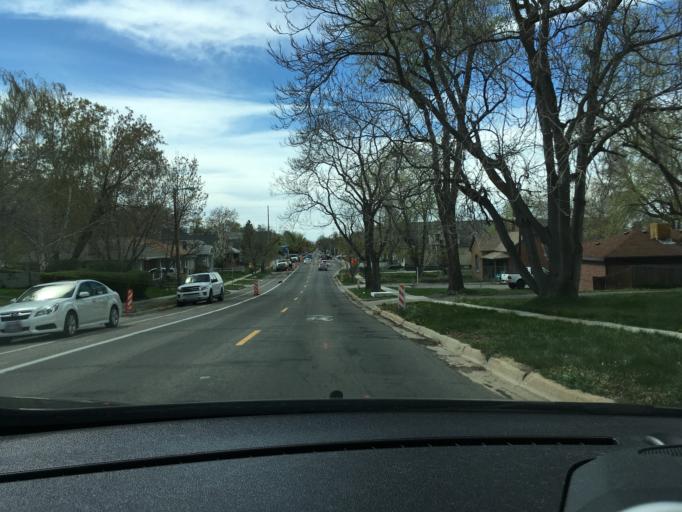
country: US
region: Utah
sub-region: Salt Lake County
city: Willard
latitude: 40.7335
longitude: -111.8572
